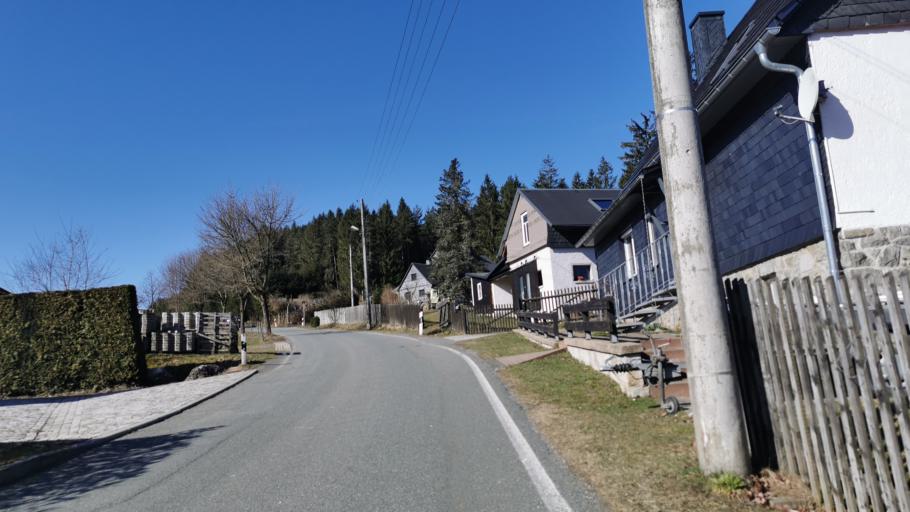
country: DE
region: Thuringia
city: Wurzbach
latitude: 50.4541
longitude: 11.5261
